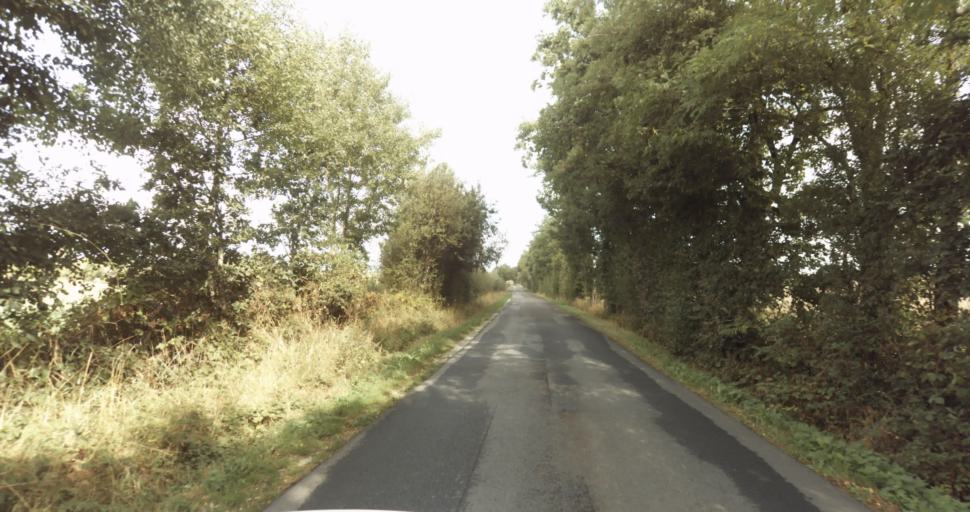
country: FR
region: Lower Normandy
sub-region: Departement de l'Orne
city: Gace
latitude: 48.8013
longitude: 0.3887
